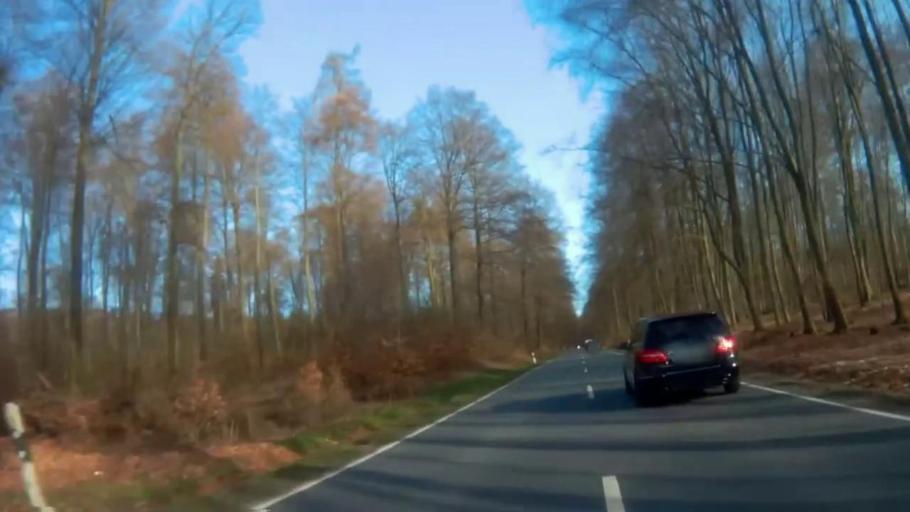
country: DE
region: Hesse
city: Gross-Bieberau
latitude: 49.8066
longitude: 8.7917
